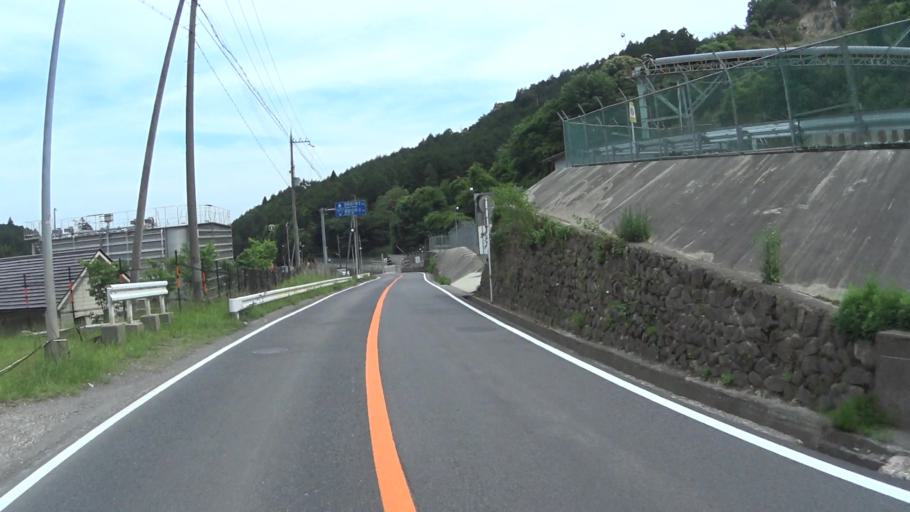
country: JP
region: Shiga Prefecture
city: Kitahama
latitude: 35.1634
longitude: 135.8617
